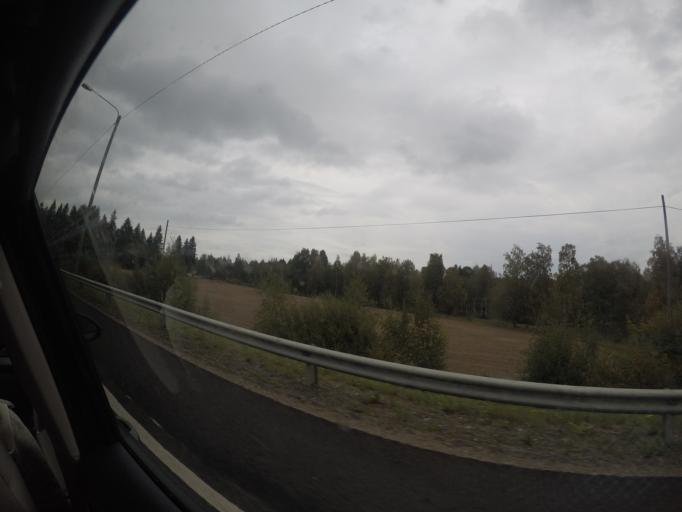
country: FI
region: Pirkanmaa
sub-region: Tampere
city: Kangasala
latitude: 61.4413
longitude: 24.1199
